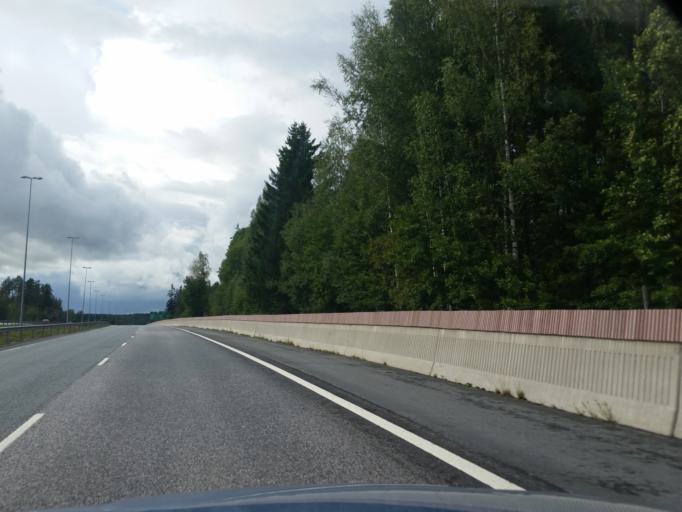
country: FI
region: Uusimaa
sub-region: Helsinki
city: Vihti
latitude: 60.3029
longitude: 24.2700
